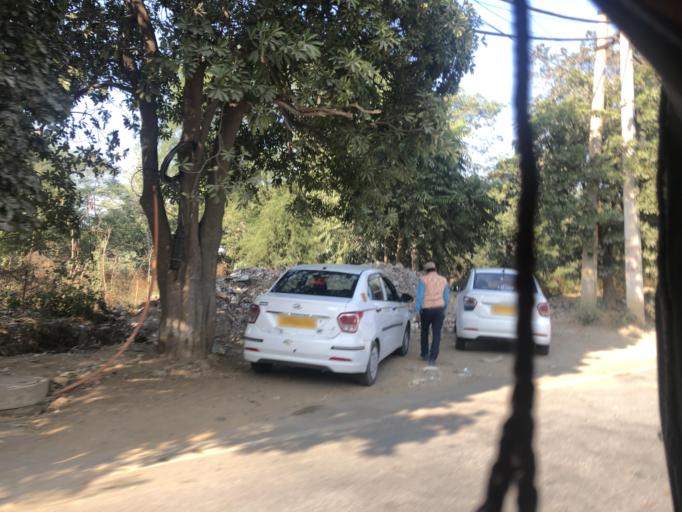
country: IN
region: Haryana
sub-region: Gurgaon
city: Gurgaon
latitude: 28.4624
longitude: 77.0692
